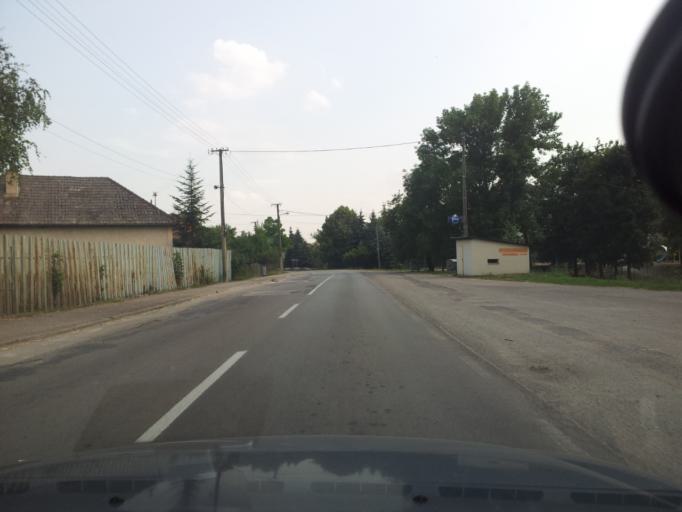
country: SK
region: Nitriansky
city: Banovce nad Bebravou
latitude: 48.7815
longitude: 18.1974
